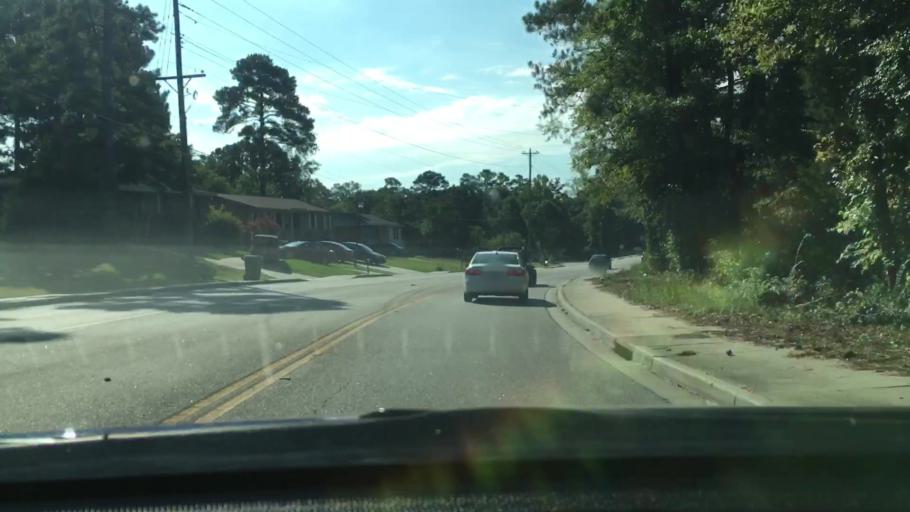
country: US
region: South Carolina
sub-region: Lexington County
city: Irmo
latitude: 34.1094
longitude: -81.1596
